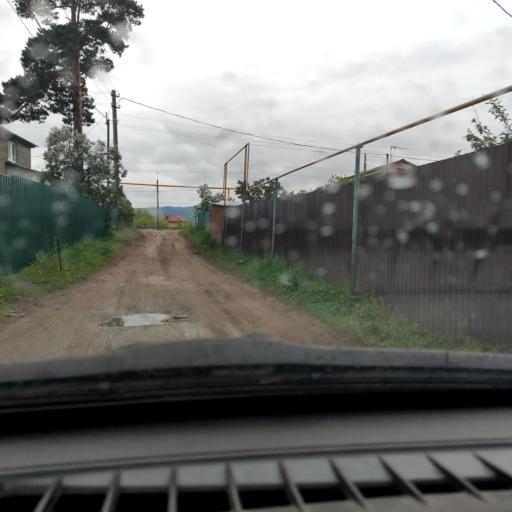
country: RU
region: Samara
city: Zhigulevsk
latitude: 53.4657
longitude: 49.5979
